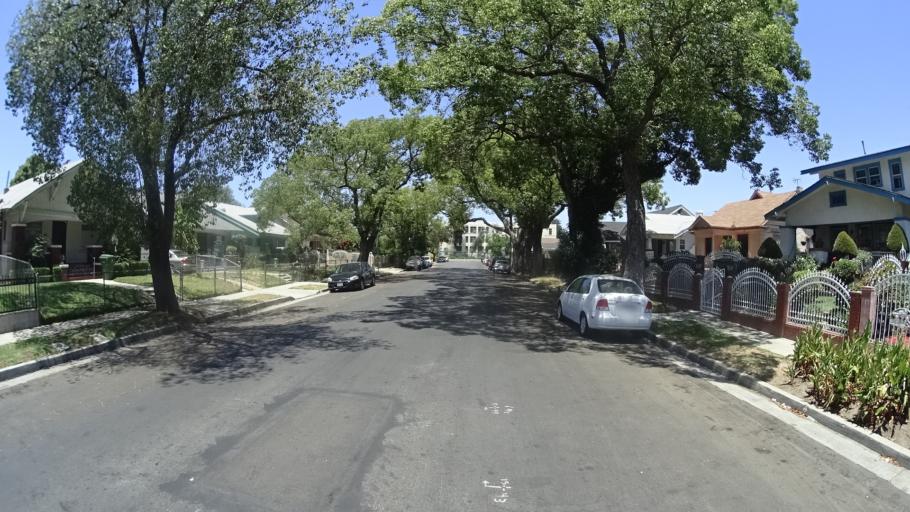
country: US
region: California
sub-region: Los Angeles County
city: View Park-Windsor Hills
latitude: 34.0170
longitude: -118.3067
